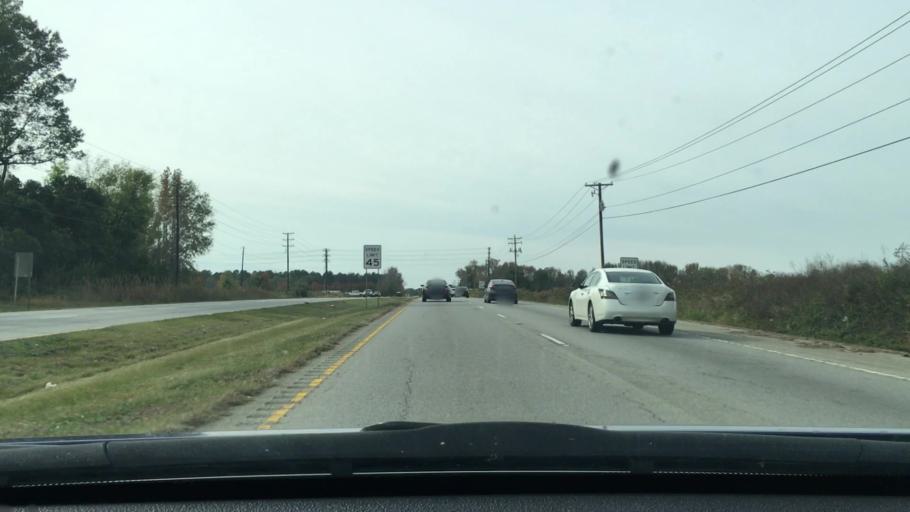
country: US
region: South Carolina
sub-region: Richland County
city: Hopkins
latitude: 33.9444
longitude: -80.8782
